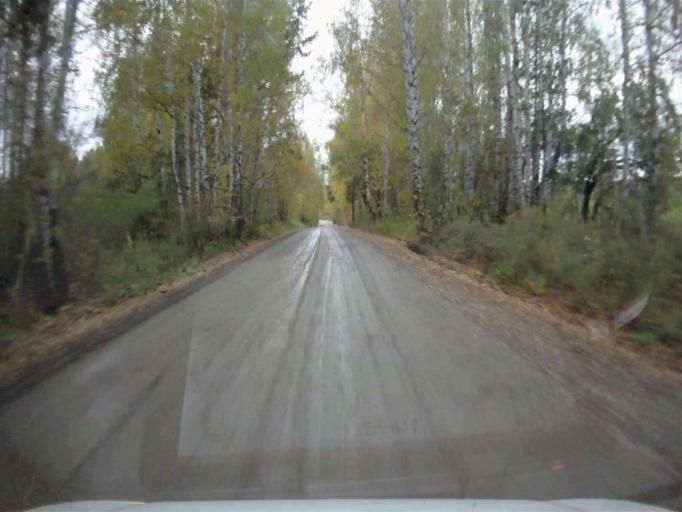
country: RU
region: Sverdlovsk
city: Mikhaylovsk
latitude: 56.1732
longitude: 59.2186
